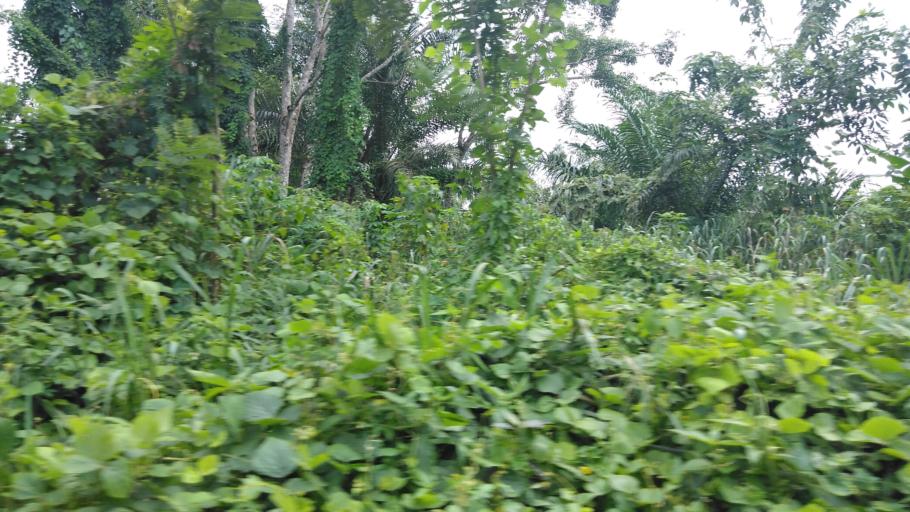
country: NG
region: Ogun
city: Abigi
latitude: 6.5953
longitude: 4.4964
